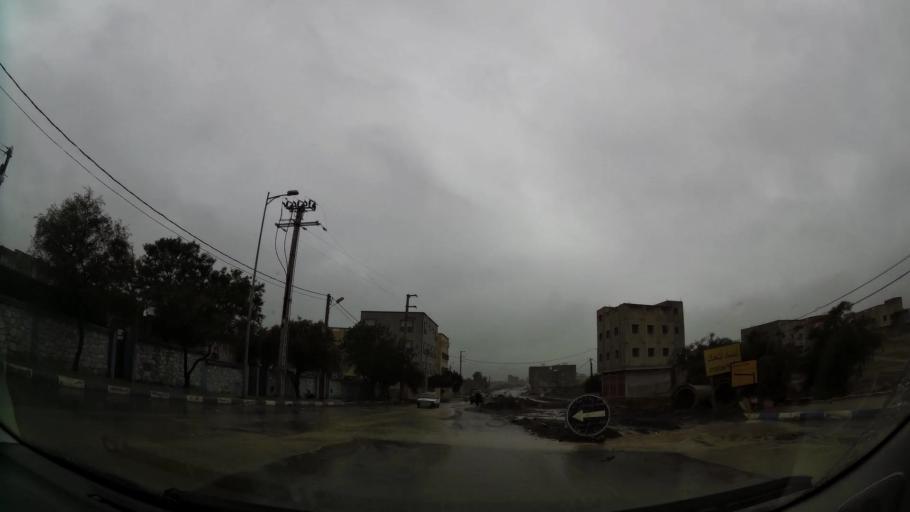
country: MA
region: Oriental
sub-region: Nador
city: Midar
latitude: 34.8822
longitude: -3.7265
